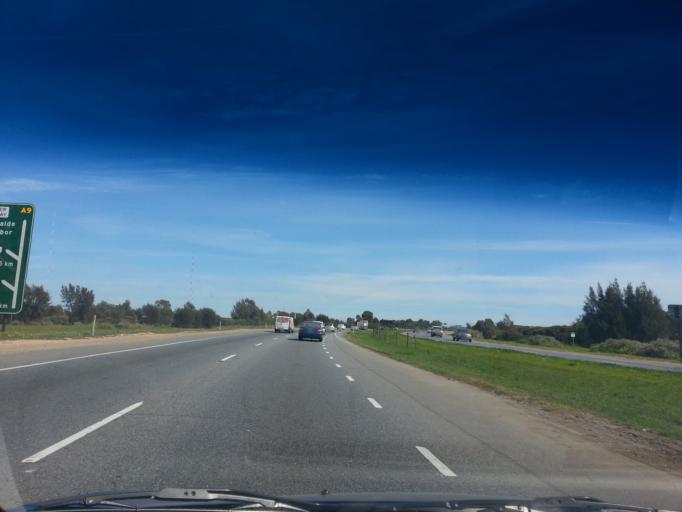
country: AU
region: South Australia
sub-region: Port Adelaide Enfield
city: Enfield
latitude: -34.8327
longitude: 138.5811
